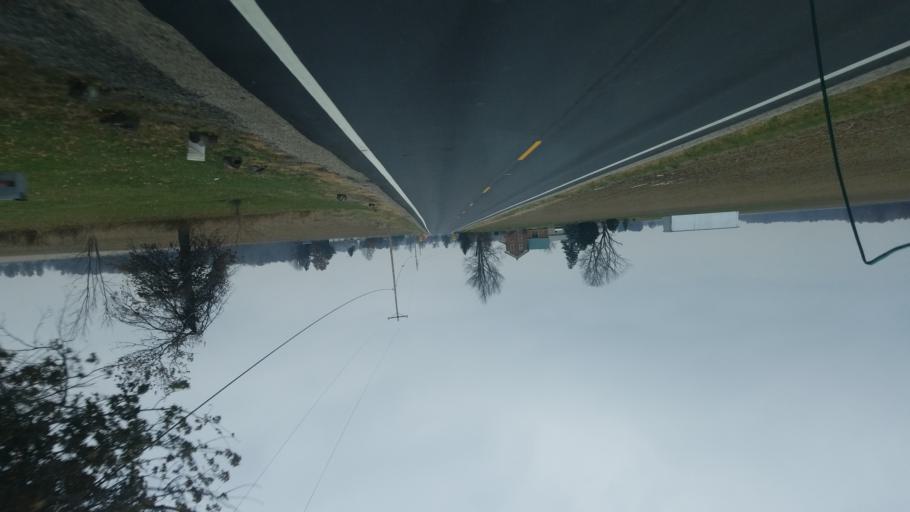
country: US
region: Ohio
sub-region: Crawford County
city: Crestline
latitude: 40.8023
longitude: -82.7878
